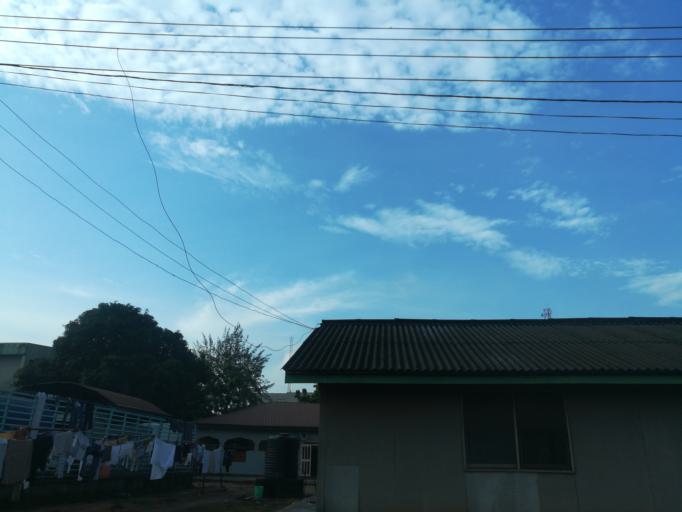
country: NG
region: Lagos
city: Ikeja
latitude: 6.5955
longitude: 3.3489
